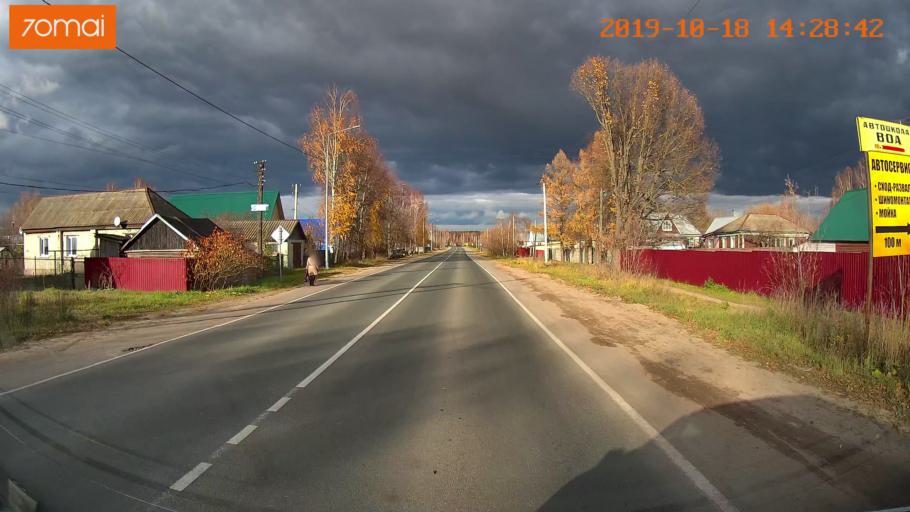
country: RU
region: Rjazan
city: Tuma
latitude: 55.1500
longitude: 40.5547
